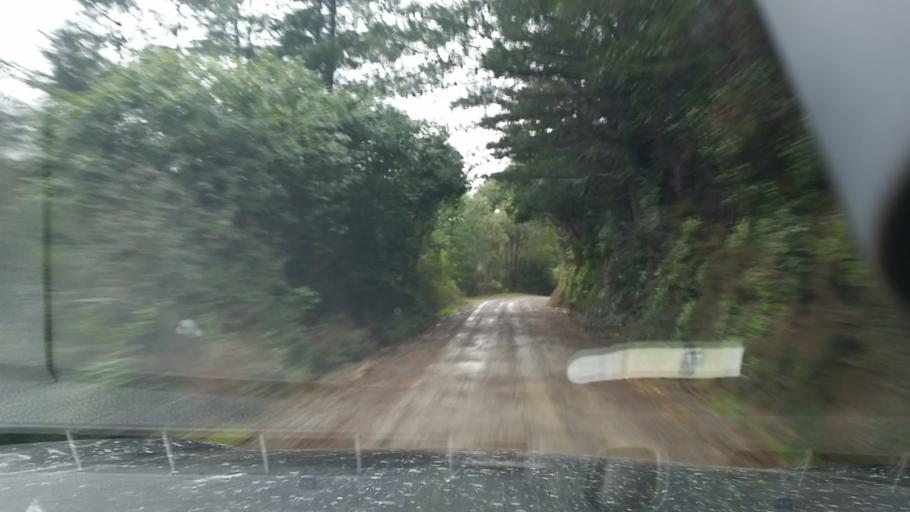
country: NZ
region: Nelson
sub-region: Nelson City
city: Nelson
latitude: -41.3611
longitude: 173.6118
